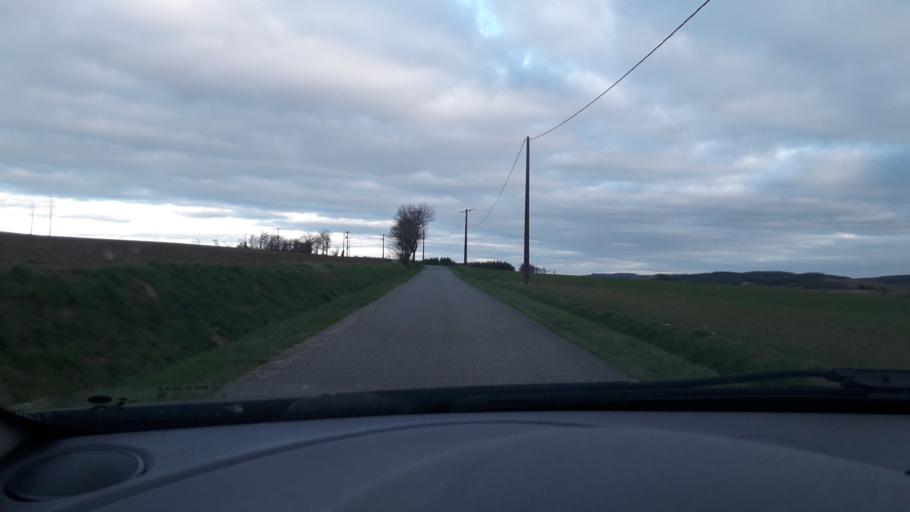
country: FR
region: Midi-Pyrenees
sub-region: Departement de la Haute-Garonne
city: Launac
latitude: 43.7043
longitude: 1.0691
